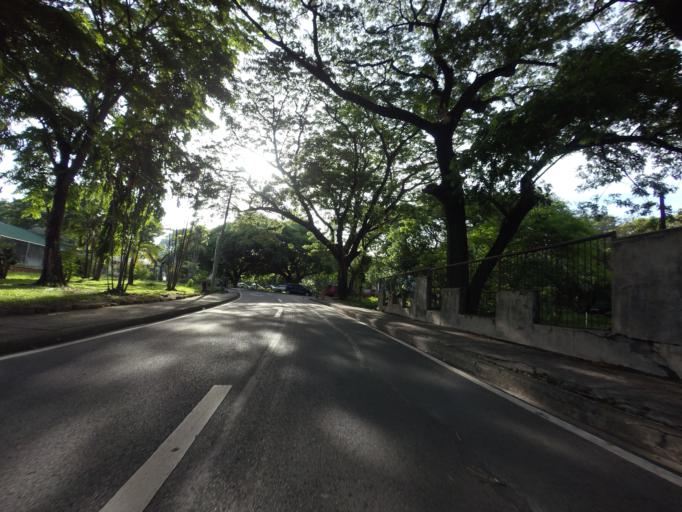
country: PH
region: Metro Manila
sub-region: Mandaluyong
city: Mandaluyong City
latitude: 14.5823
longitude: 121.0430
